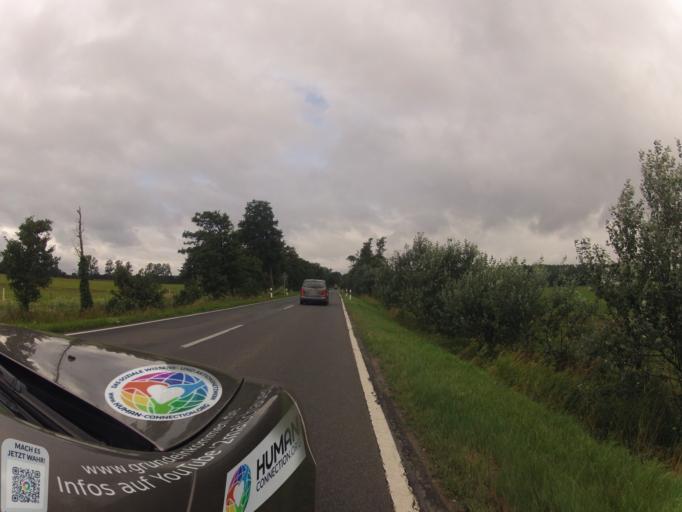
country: DE
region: Mecklenburg-Vorpommern
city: Lassan
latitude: 53.8786
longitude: 13.7994
